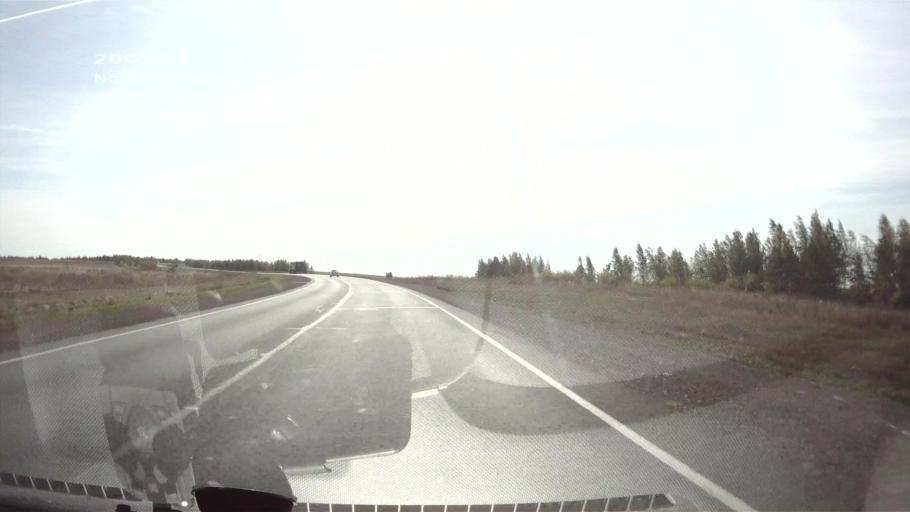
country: RU
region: Samara
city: Syzran'
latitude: 52.9444
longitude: 48.3043
